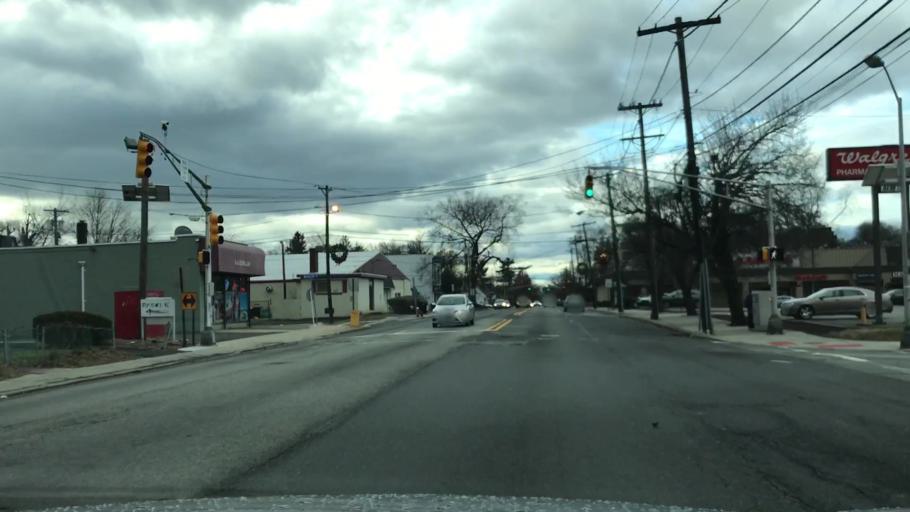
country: US
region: New Jersey
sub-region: Bergen County
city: Teaneck
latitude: 40.9011
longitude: -73.9995
